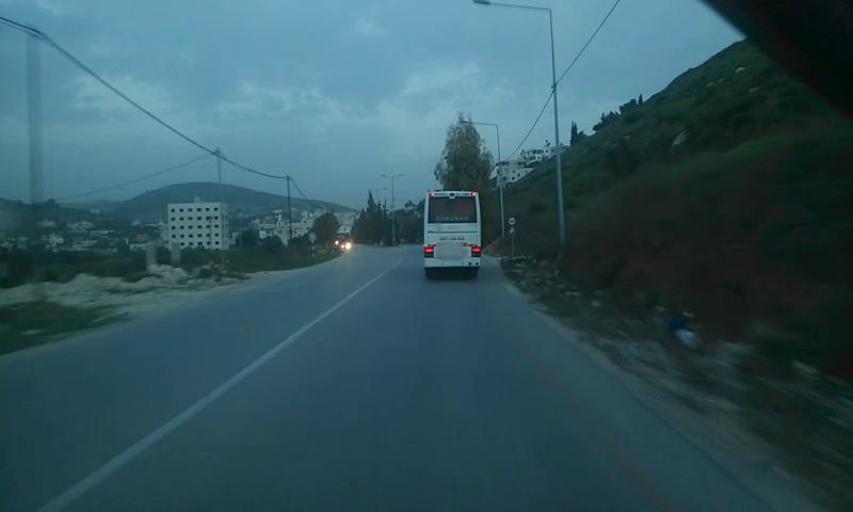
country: PS
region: West Bank
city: `Anabta
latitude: 32.3105
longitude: 35.1058
